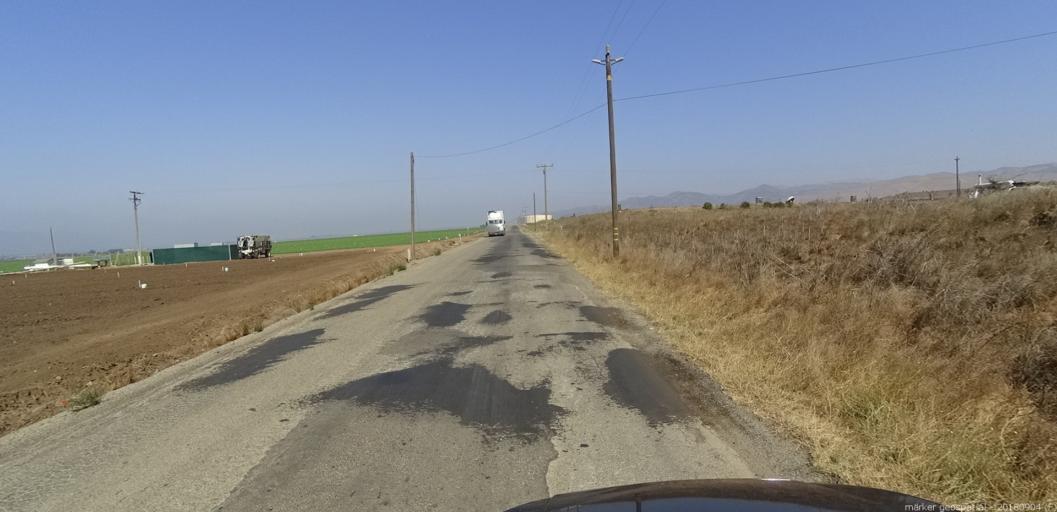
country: US
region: California
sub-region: Monterey County
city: Gonzales
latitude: 36.5203
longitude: -121.4134
